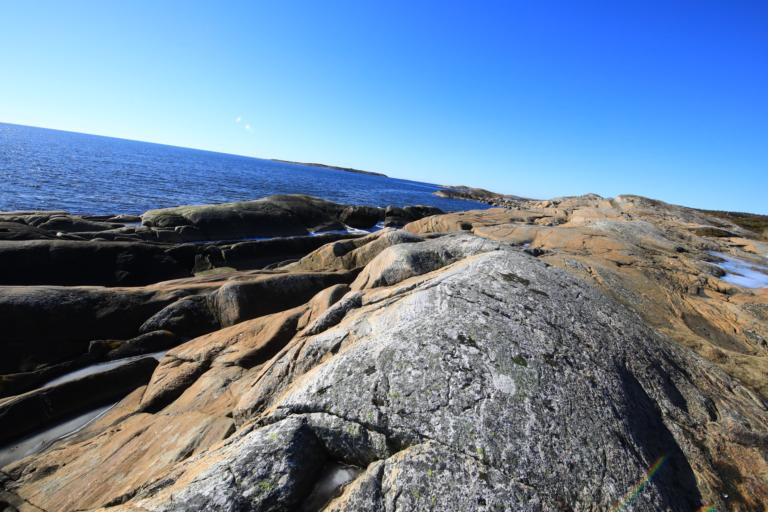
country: SE
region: Halland
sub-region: Kungsbacka Kommun
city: Frillesas
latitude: 57.2257
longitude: 12.1229
